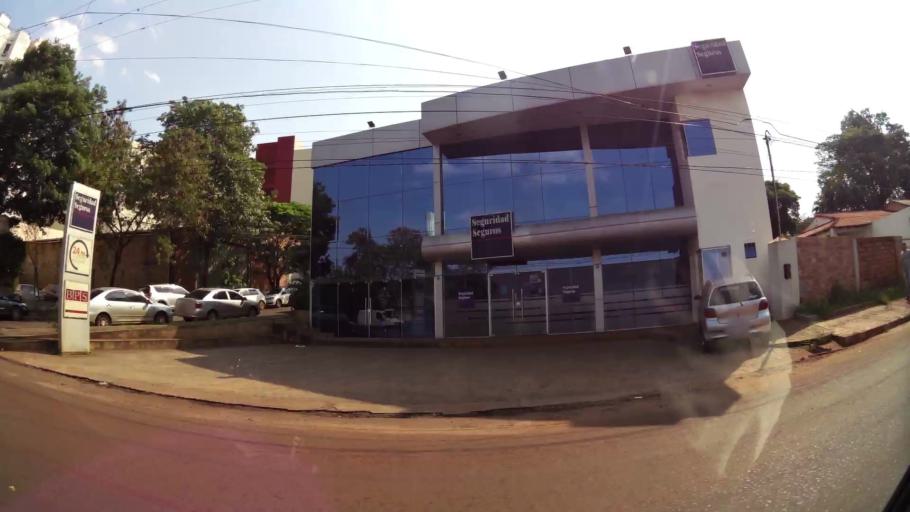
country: PY
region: Alto Parana
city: Ciudad del Este
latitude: -25.5091
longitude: -54.6218
